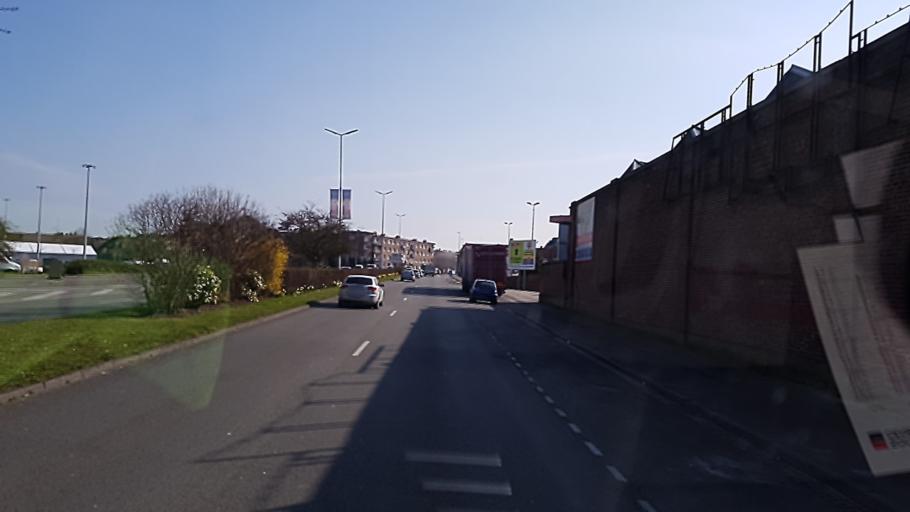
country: FR
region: Nord-Pas-de-Calais
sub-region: Departement du Nord
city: Neuville-en-Ferrain
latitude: 50.7375
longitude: 3.1592
